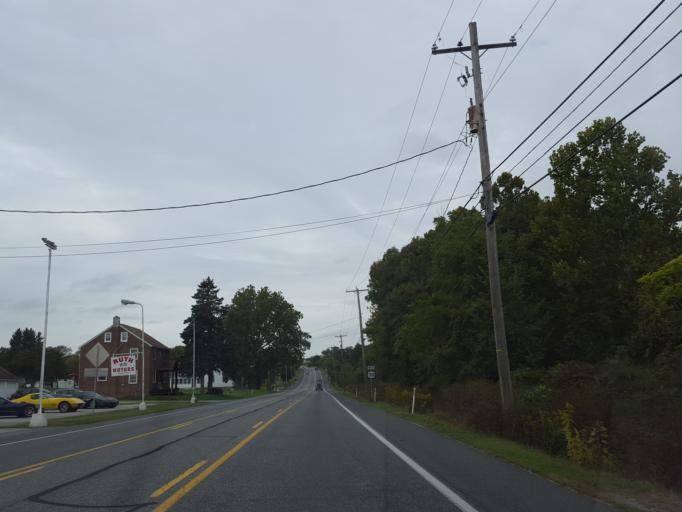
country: US
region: Pennsylvania
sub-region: York County
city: Spring Grove
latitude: 39.9207
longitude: -76.8983
